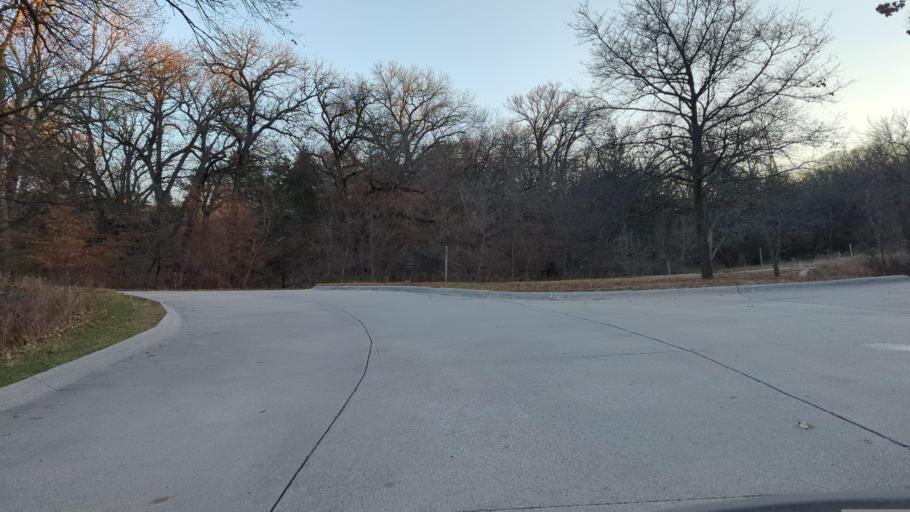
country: US
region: Nebraska
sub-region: Cass County
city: Louisville
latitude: 40.9872
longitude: -96.2194
